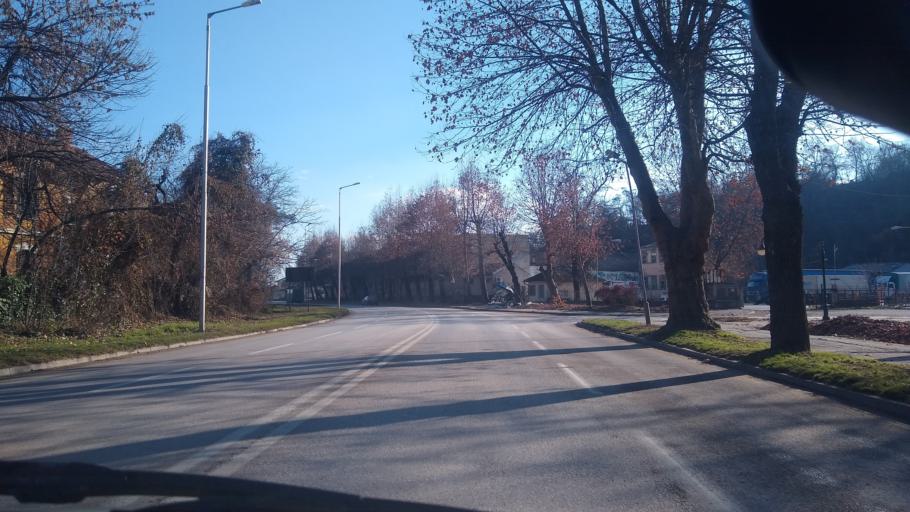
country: MK
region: Bitola
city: Bitola
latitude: 41.0174
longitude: 21.3424
